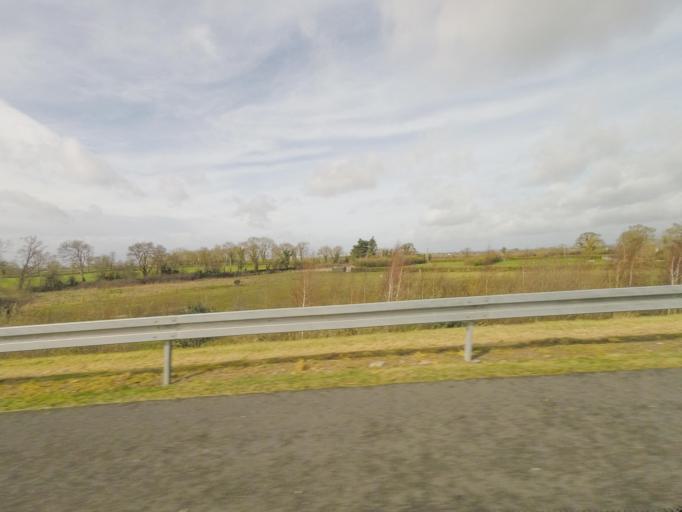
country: IE
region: Leinster
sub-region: Kilkenny
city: Kilkenny
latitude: 52.6292
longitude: -7.1522
